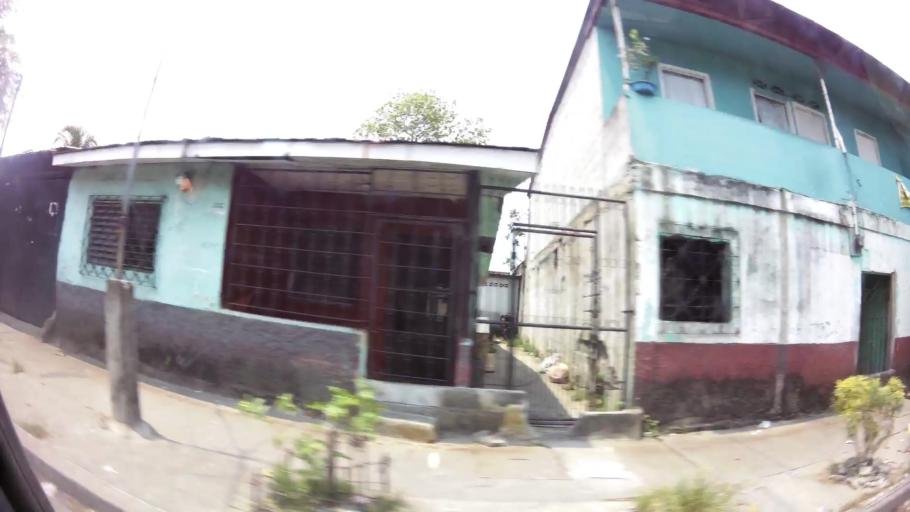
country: HN
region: Cortes
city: San Pedro Sula
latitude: 15.4905
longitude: -88.0141
